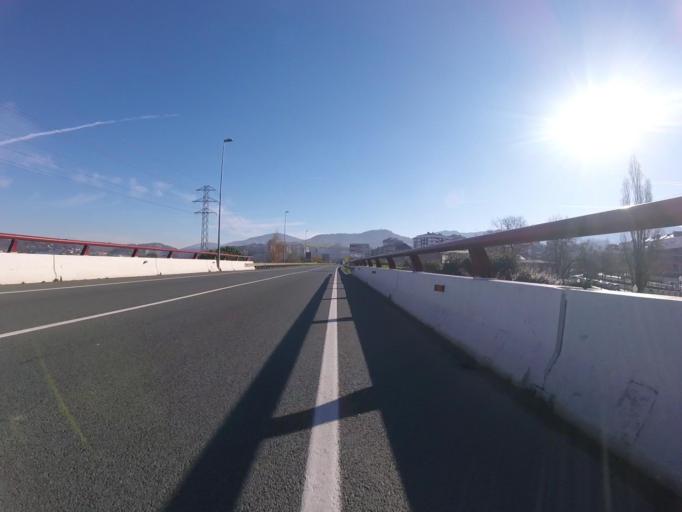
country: ES
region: Basque Country
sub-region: Provincia de Guipuzcoa
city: Irun
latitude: 43.3431
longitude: -1.7857
